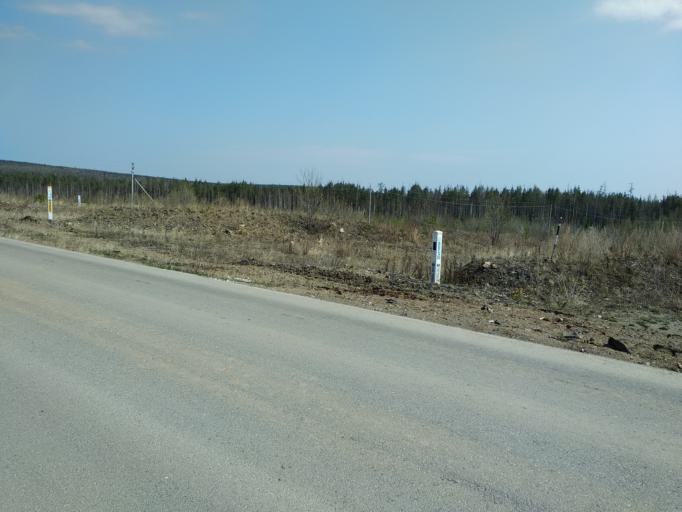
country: RU
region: Sverdlovsk
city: Karpinsk
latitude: 59.6221
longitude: 59.5904
